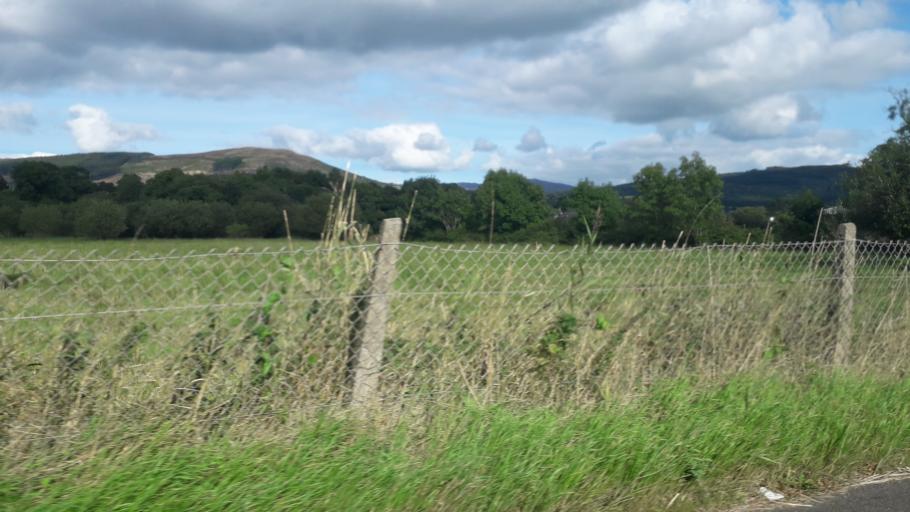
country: IE
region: Leinster
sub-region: Lu
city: Blackrock
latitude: 54.0178
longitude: -6.3269
